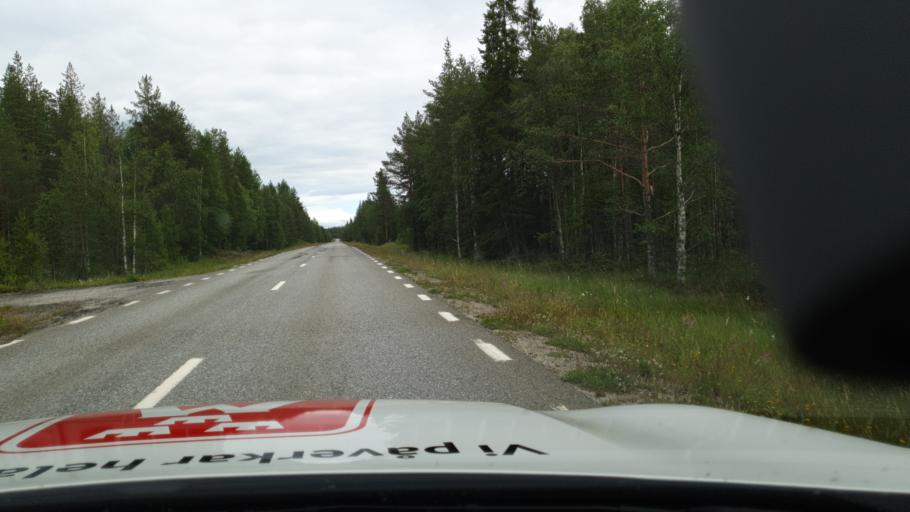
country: SE
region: Vaesterbotten
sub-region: Lycksele Kommun
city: Soderfors
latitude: 64.6200
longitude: 18.1471
